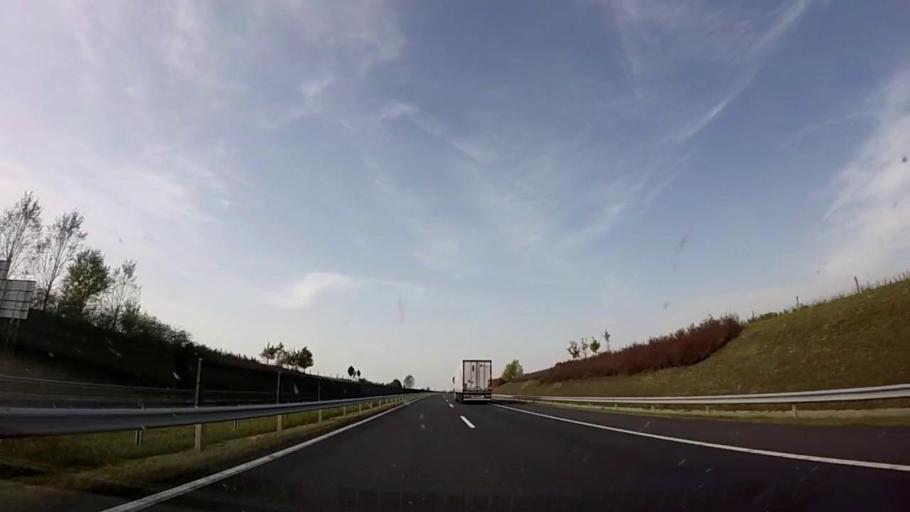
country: HU
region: Zala
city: Nagykanizsa
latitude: 46.4761
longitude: 17.0220
